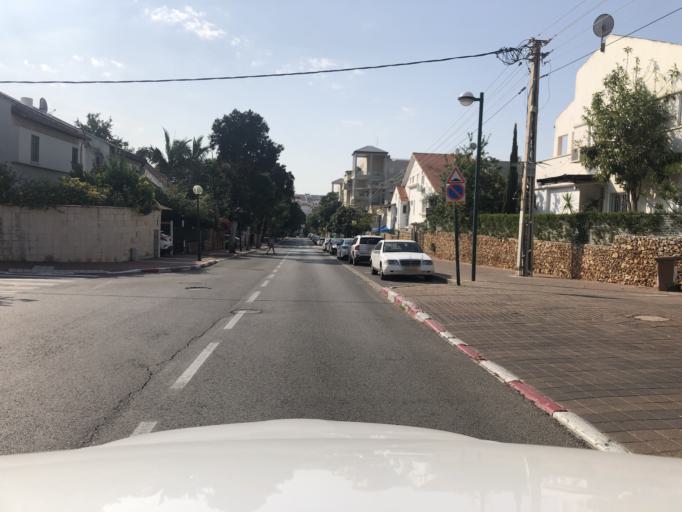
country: IL
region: Central District
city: Kfar Saba
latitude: 32.1819
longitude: 34.9071
